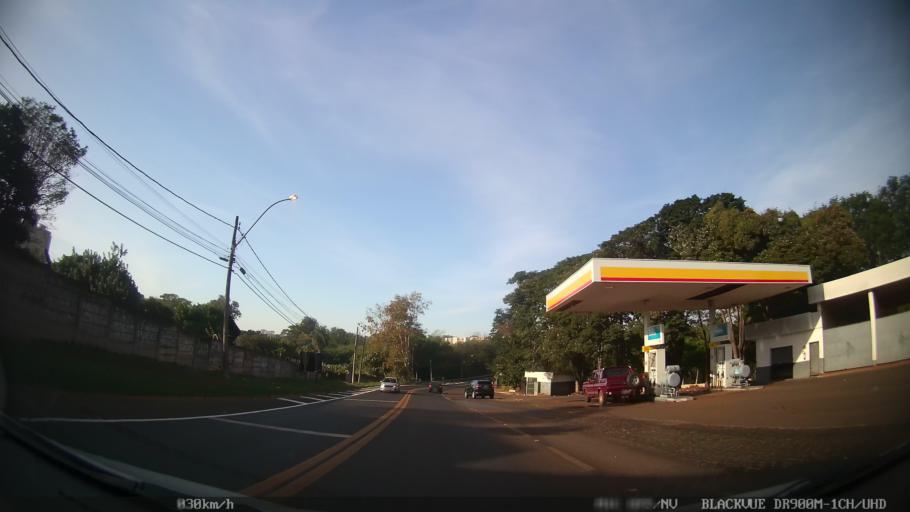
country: BR
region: Sao Paulo
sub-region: Ribeirao Preto
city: Ribeirao Preto
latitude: -21.2678
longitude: -47.8175
